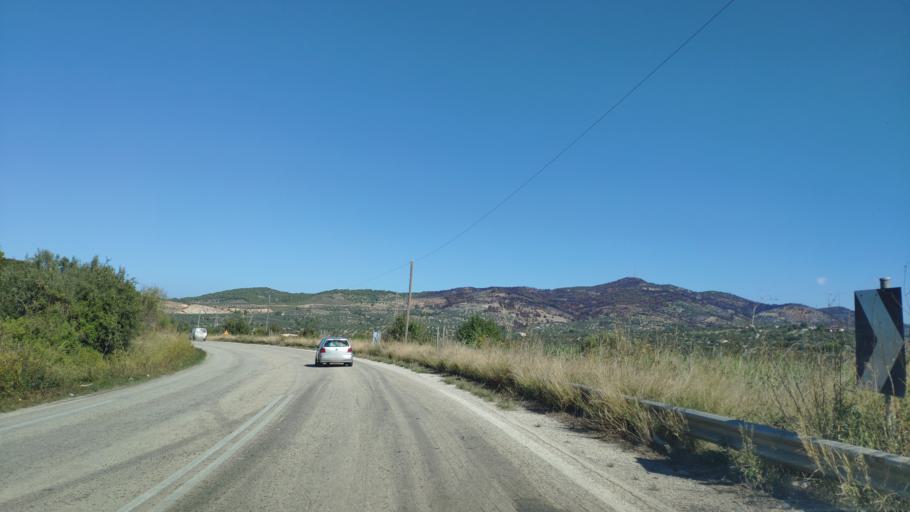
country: GR
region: Peloponnese
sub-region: Nomos Korinthias
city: Athikia
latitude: 37.8385
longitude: 22.8995
